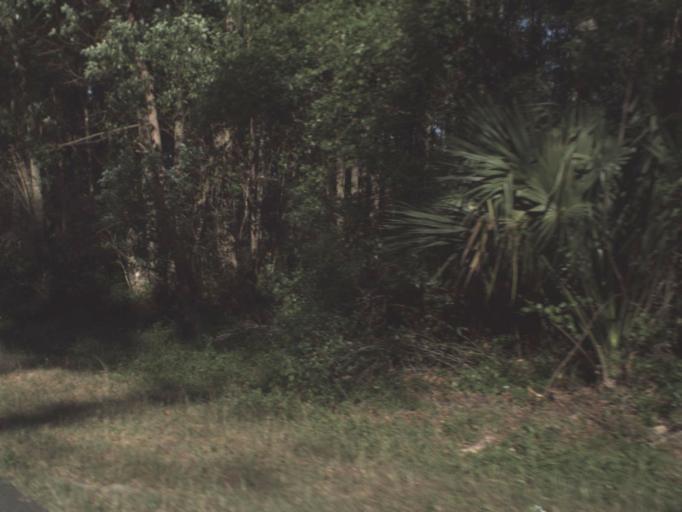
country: US
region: Florida
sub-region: Marion County
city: Dunnellon
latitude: 29.1487
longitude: -82.3689
